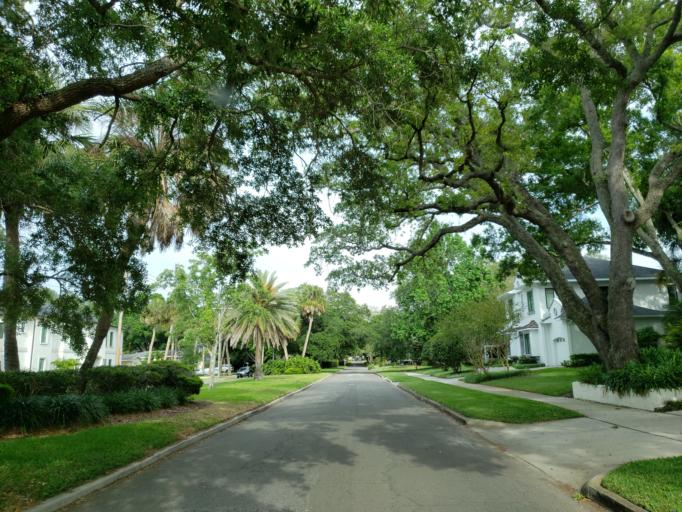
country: US
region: Florida
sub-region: Hillsborough County
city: Tampa
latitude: 27.9376
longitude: -82.5180
